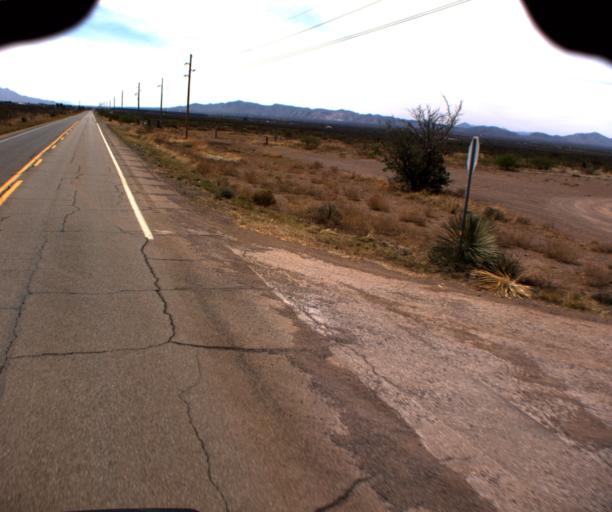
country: US
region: Arizona
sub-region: Cochise County
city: Pirtleville
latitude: 31.3875
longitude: -109.5793
